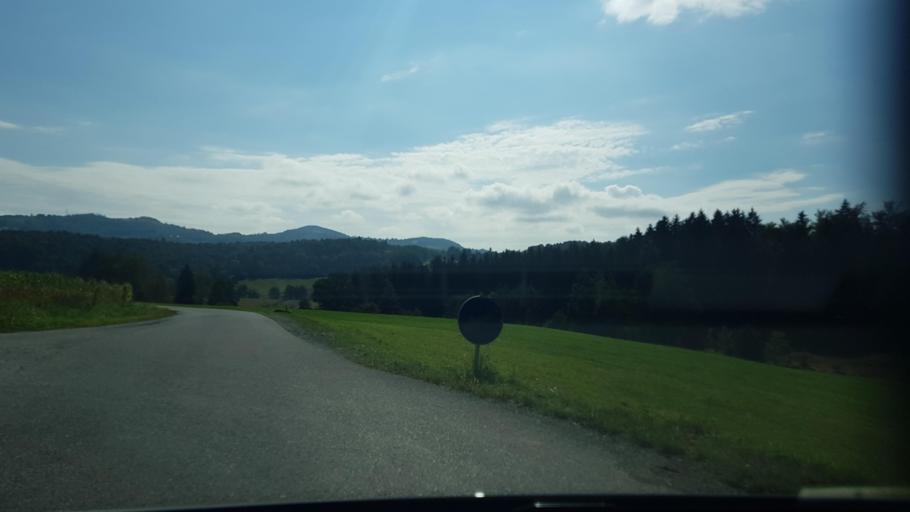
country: AT
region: Styria
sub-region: Politischer Bezirk Deutschlandsberg
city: Wettmannstatten
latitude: 46.8120
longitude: 15.3803
